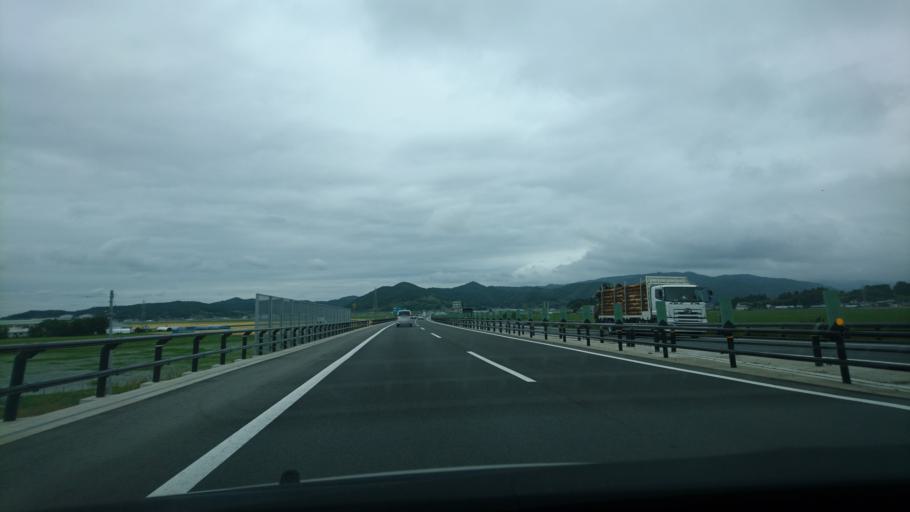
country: JP
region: Miyagi
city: Ishinomaki
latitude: 38.5064
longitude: 141.2863
